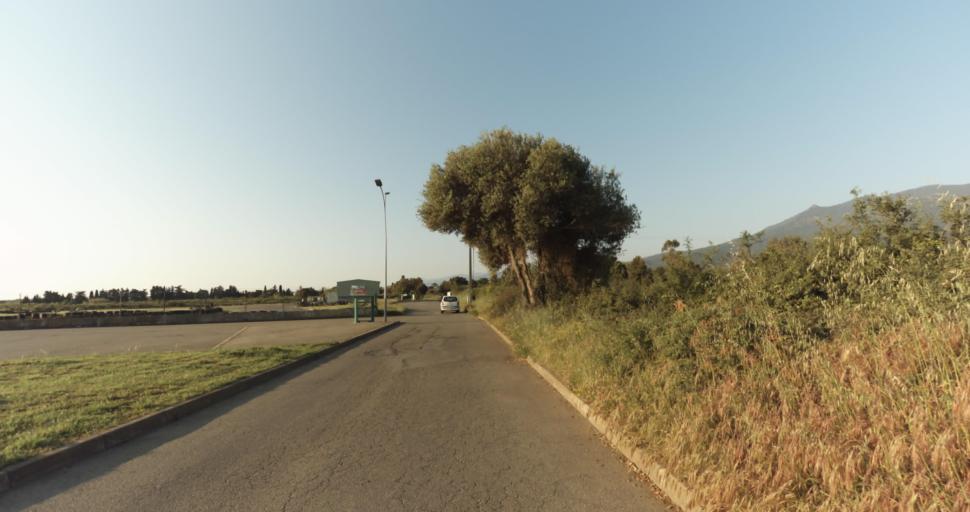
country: FR
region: Corsica
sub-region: Departement de la Haute-Corse
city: Biguglia
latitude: 42.6075
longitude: 9.4439
